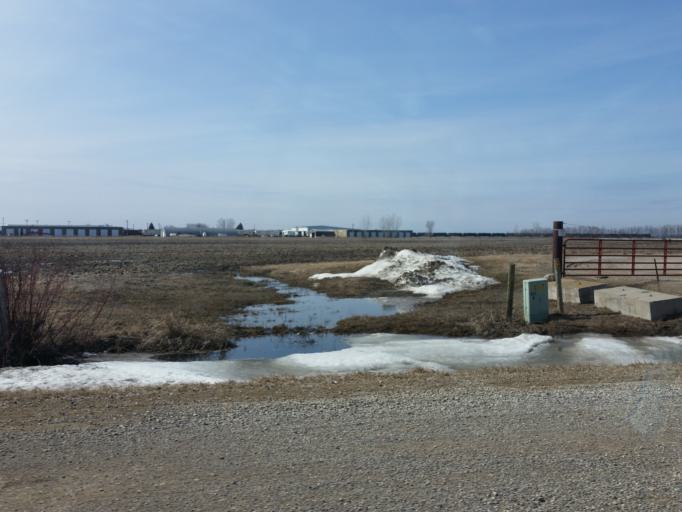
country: US
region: North Dakota
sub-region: Walsh County
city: Grafton
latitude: 48.4306
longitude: -97.4055
